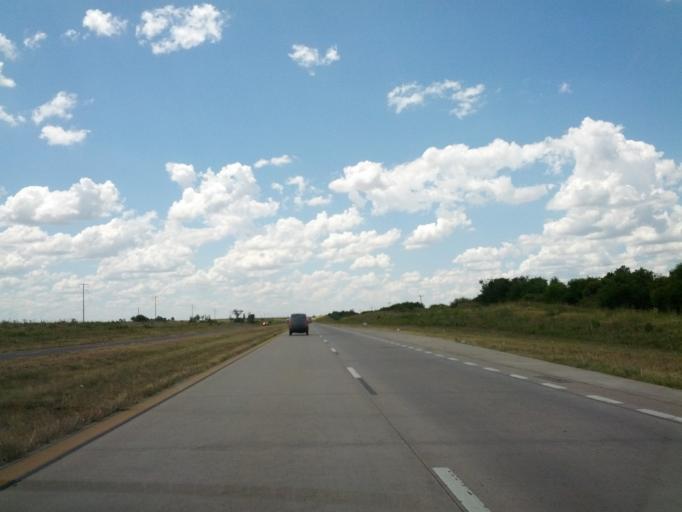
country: AR
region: Entre Rios
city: Gualeguaychu
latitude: -32.9300
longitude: -58.5710
